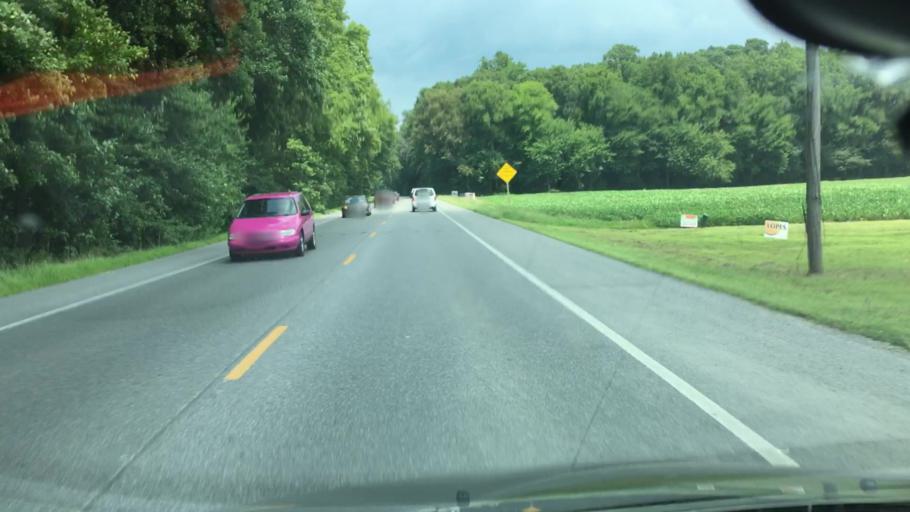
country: US
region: Maryland
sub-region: Worcester County
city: Ocean Pines
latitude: 38.3648
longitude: -75.1668
